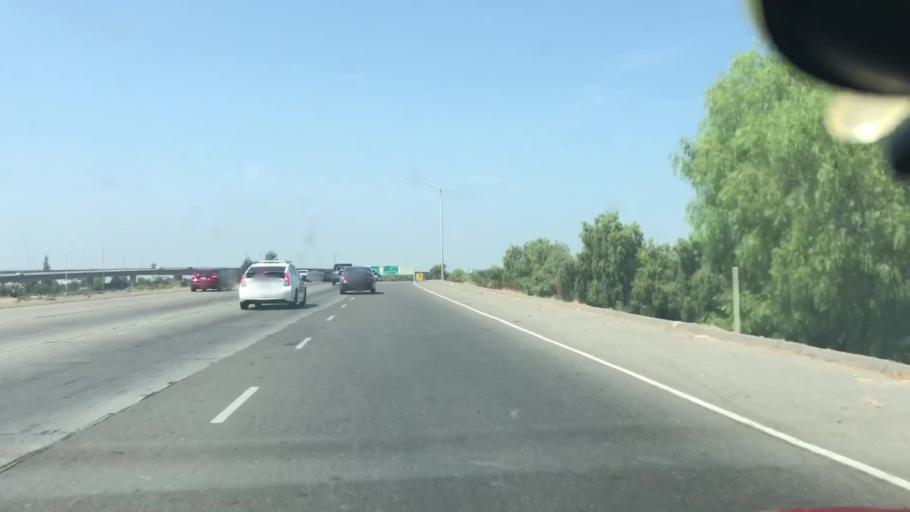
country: US
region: California
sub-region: San Joaquin County
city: Stockton
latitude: 37.9490
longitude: -121.2925
